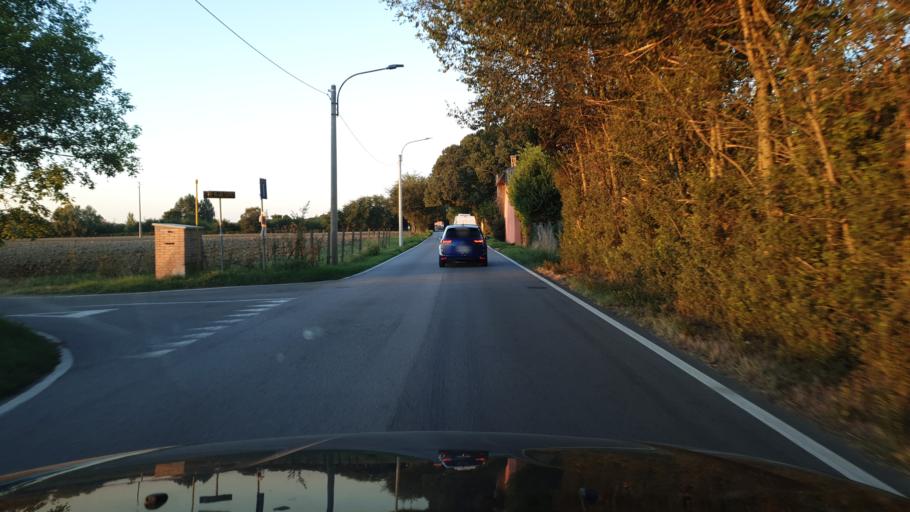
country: IT
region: Emilia-Romagna
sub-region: Provincia di Bologna
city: Quarto Inferiore
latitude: 44.5341
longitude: 11.3894
